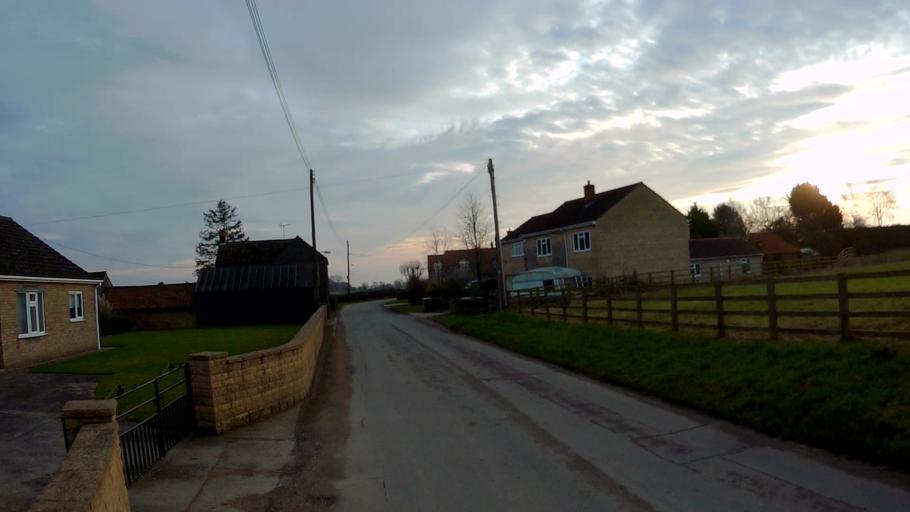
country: GB
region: England
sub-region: Lincolnshire
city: Bourne
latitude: 52.8123
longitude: -0.3986
